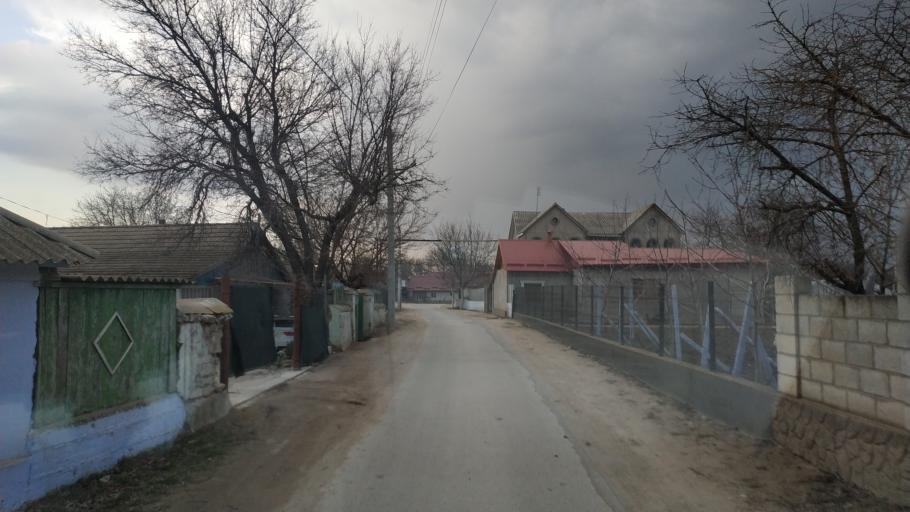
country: MD
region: Telenesti
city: Grigoriopol
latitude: 47.0257
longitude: 29.3492
